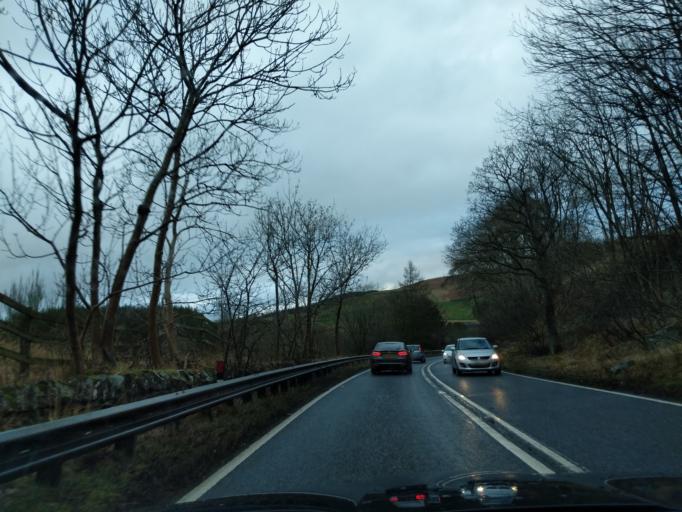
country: GB
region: Scotland
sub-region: The Scottish Borders
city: Galashiels
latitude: 55.6567
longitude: -2.8690
